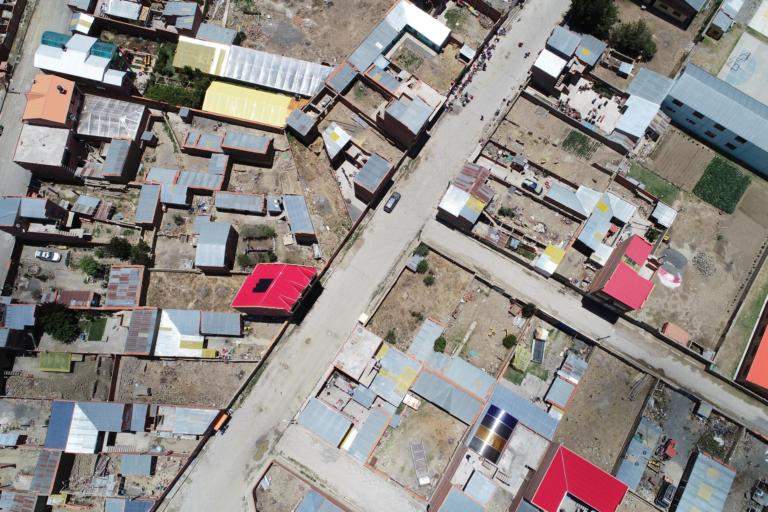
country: BO
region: La Paz
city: Achacachi
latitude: -16.0484
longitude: -68.6876
